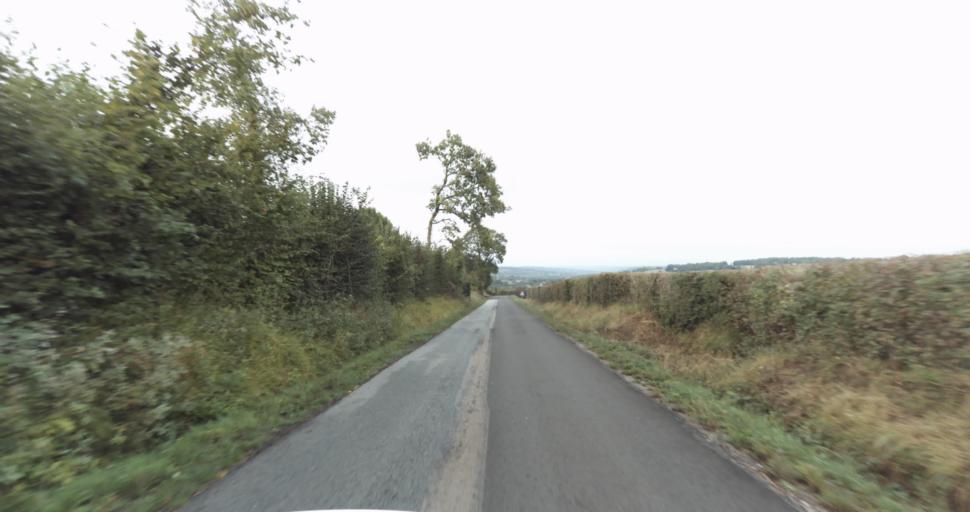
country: FR
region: Lower Normandy
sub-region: Departement de l'Orne
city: Trun
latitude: 48.9081
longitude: 0.1036
